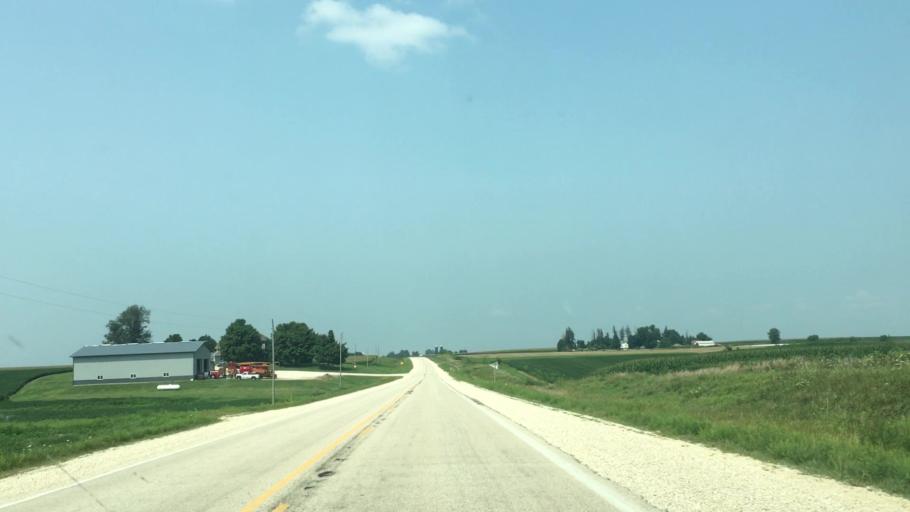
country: US
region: Iowa
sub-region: Fayette County
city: West Union
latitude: 42.9896
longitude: -91.8240
